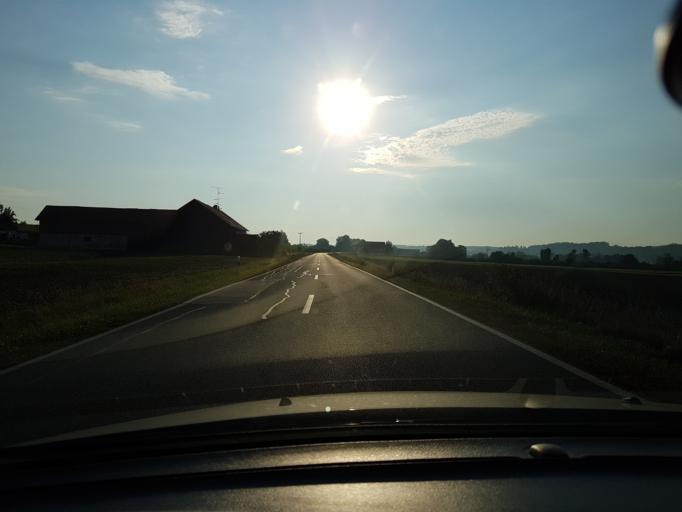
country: DE
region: Bavaria
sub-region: Lower Bavaria
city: Schalkham
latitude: 48.4982
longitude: 12.4053
